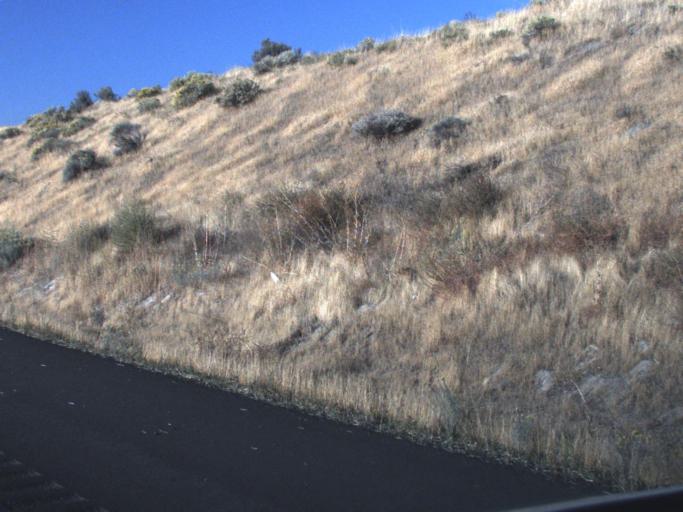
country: US
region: Washington
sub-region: Franklin County
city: Connell
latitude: 46.6670
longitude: -118.8484
